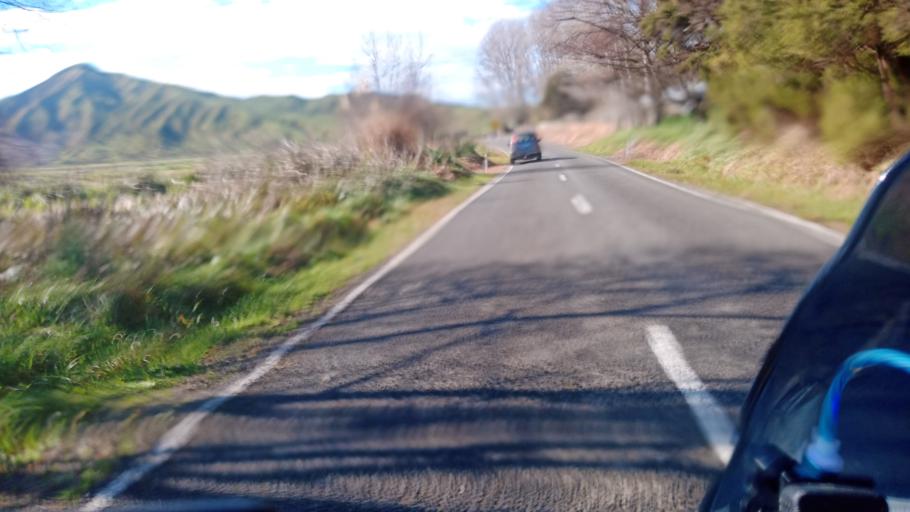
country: NZ
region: Gisborne
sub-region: Gisborne District
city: Gisborne
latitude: -38.2733
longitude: 178.2753
